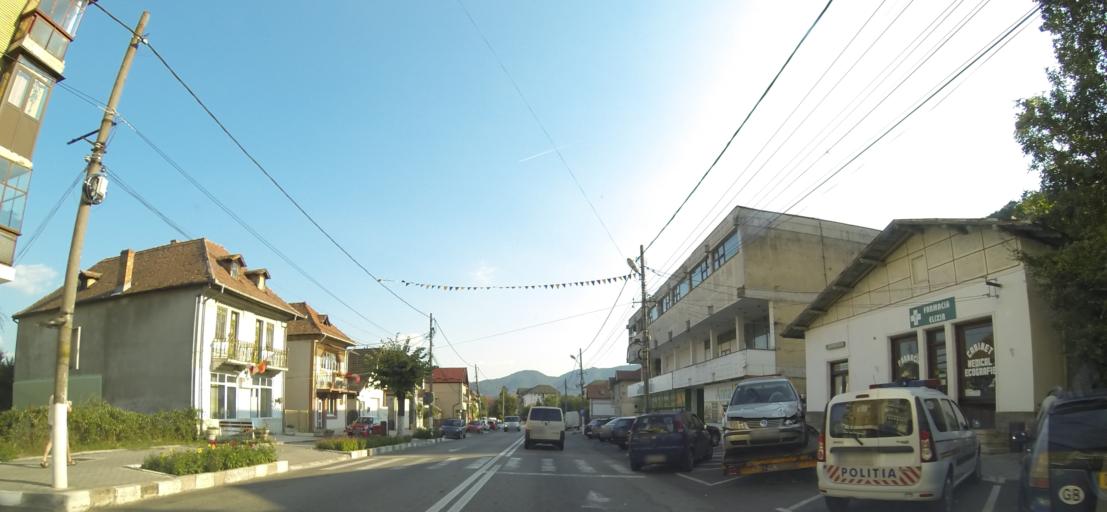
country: RO
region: Valcea
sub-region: Oras Calimanesti
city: Jiblea Veche
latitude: 45.2451
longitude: 24.3394
